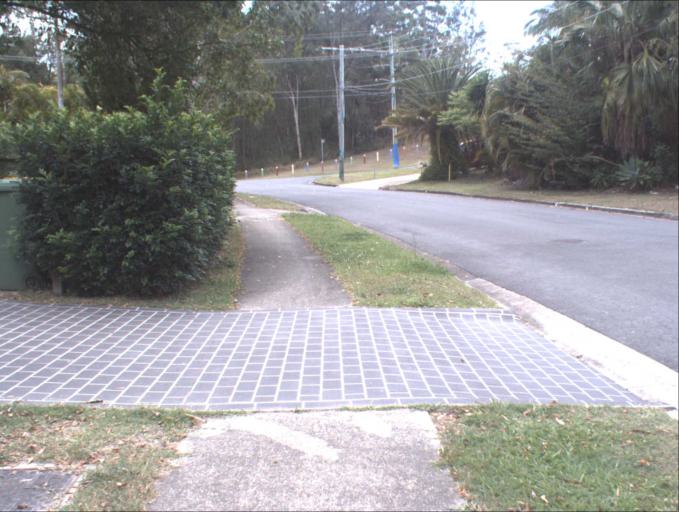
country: AU
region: Queensland
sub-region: Logan
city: Slacks Creek
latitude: -27.6409
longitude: 153.1698
